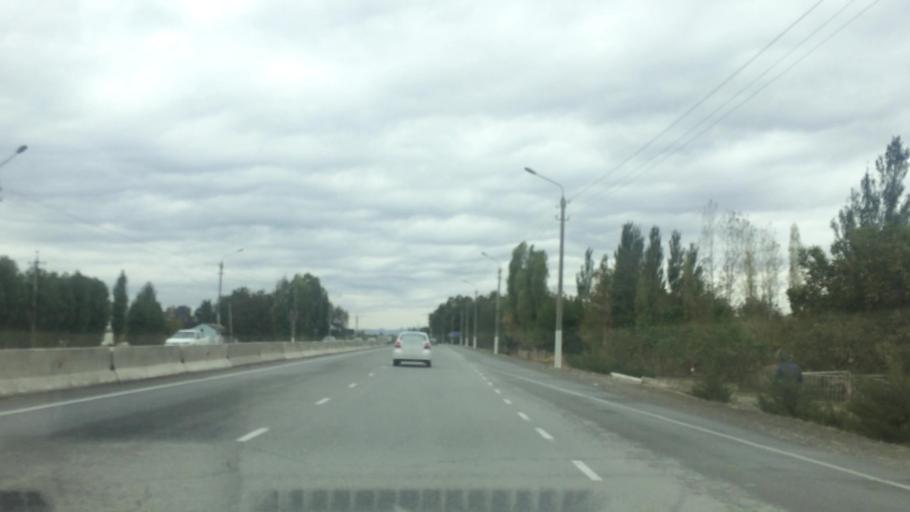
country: UZ
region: Jizzax
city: Jizzax
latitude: 39.9790
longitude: 67.5663
